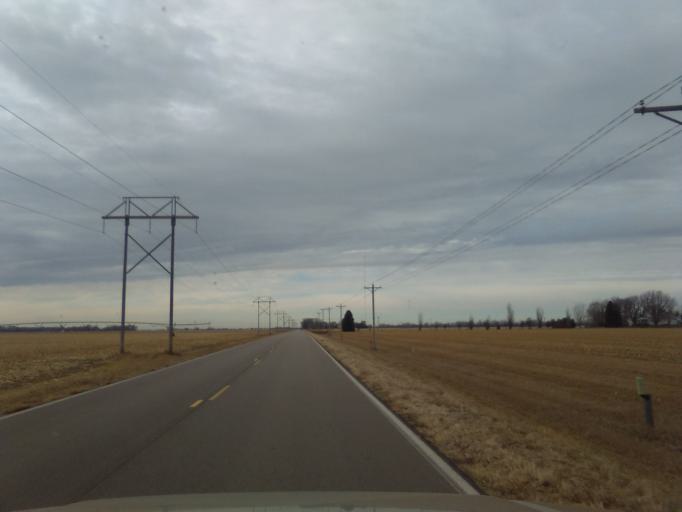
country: US
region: Nebraska
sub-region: Buffalo County
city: Gibbon
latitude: 40.6550
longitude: -98.8319
